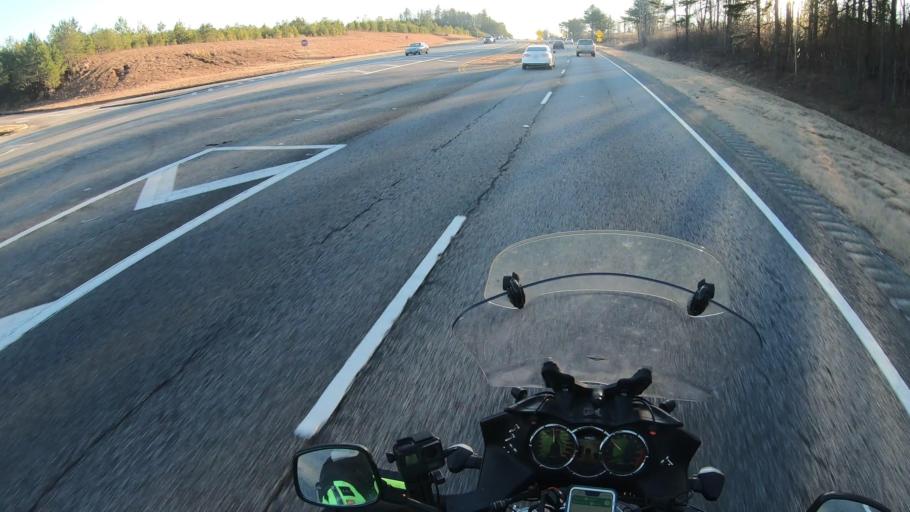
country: US
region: Georgia
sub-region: Lumpkin County
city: Dahlonega
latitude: 34.4639
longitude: -83.9719
